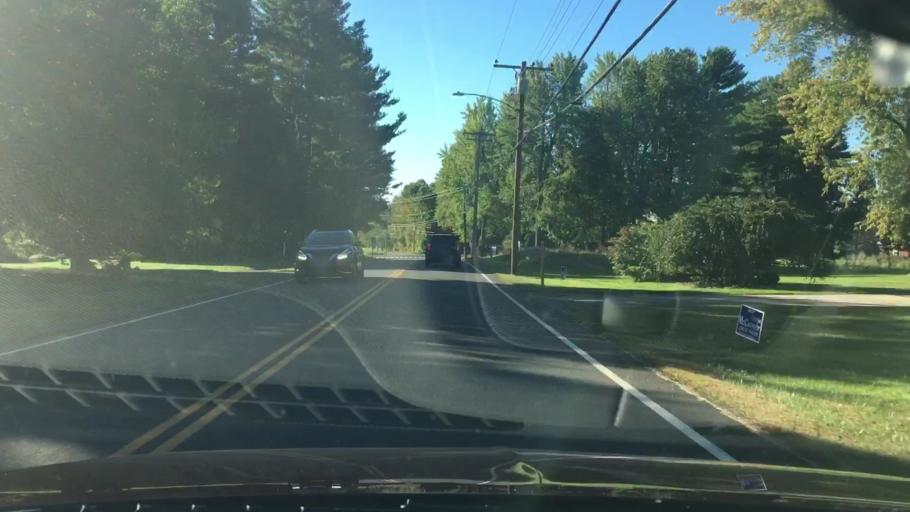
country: US
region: Connecticut
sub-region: Hartford County
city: Sherwood Manor
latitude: 42.0060
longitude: -72.5592
